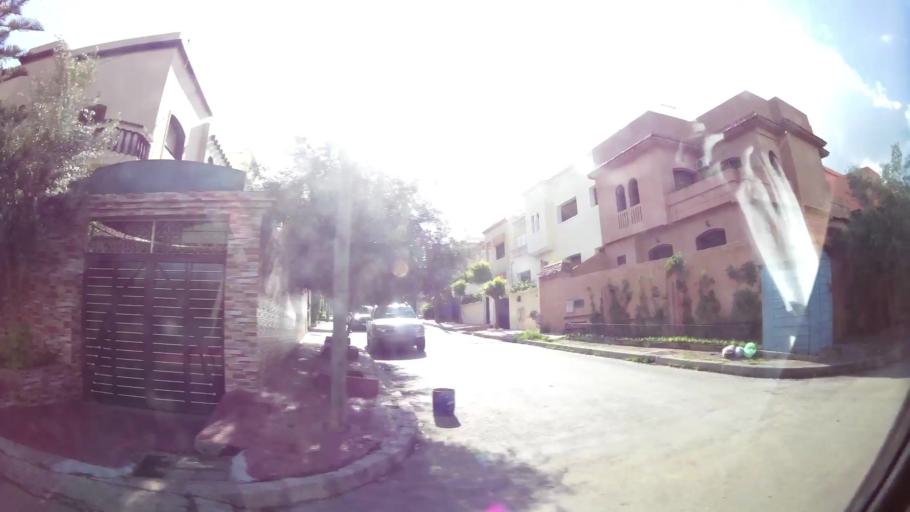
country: MA
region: Chaouia-Ouardigha
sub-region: Settat Province
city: Settat
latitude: 33.0094
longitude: -7.6286
